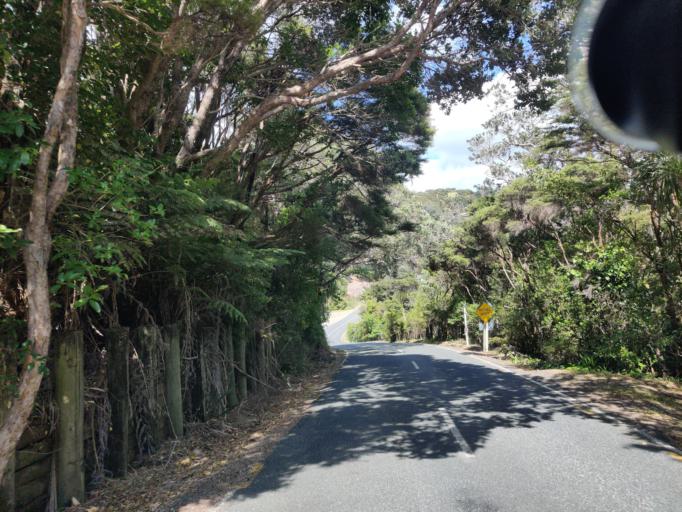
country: NZ
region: Northland
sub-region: Far North District
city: Paihia
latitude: -35.2572
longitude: 174.2440
